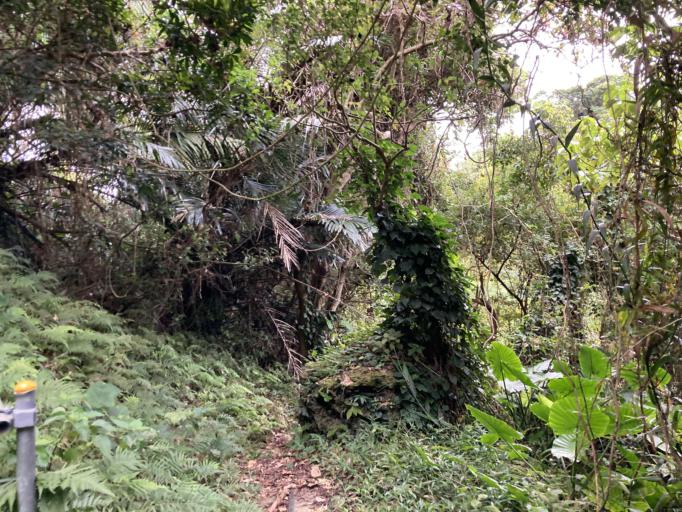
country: JP
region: Okinawa
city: Okinawa
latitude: 26.3914
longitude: 127.7584
